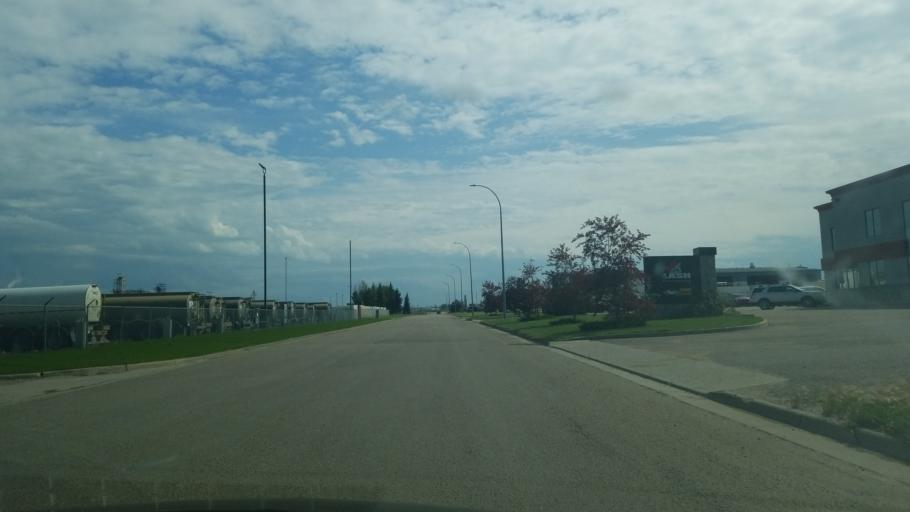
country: CA
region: Saskatchewan
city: Lloydminster
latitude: 53.2900
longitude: -110.0368
